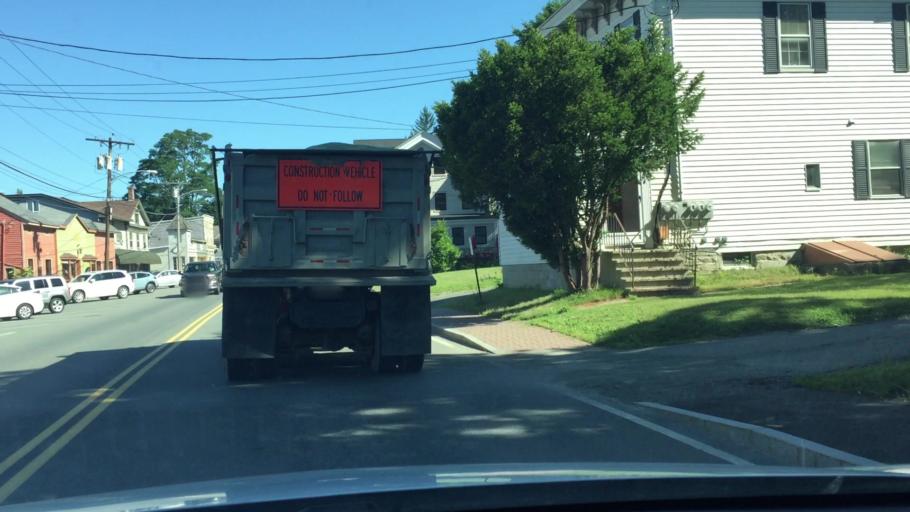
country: US
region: Massachusetts
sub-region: Berkshire County
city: West Stockbridge
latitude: 42.3330
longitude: -73.3668
